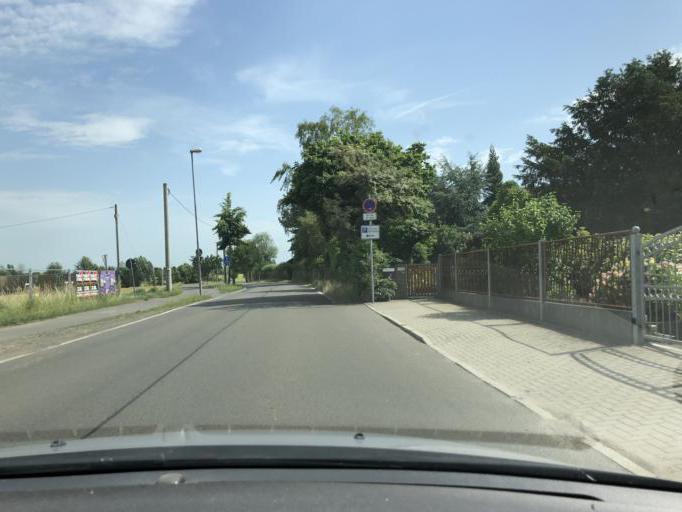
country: DE
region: Saxony
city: Taucha
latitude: 51.3754
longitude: 12.4979
